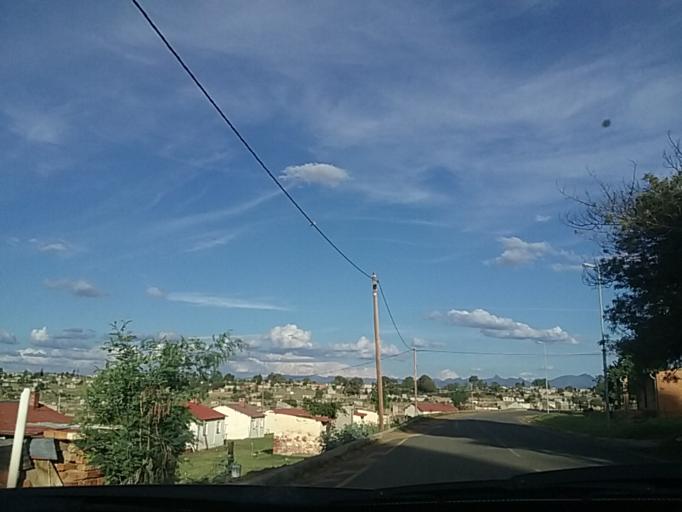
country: LS
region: Berea
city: Teyateyaneng
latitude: -29.1429
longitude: 27.7409
